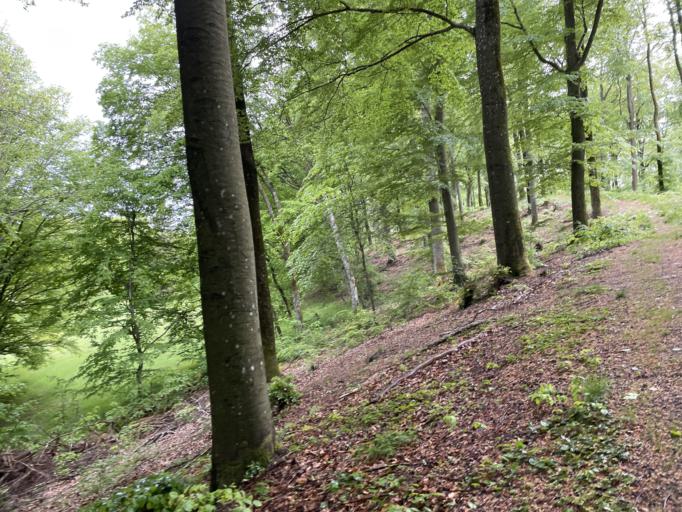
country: SE
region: Skane
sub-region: Hassleholms Kommun
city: Sosdala
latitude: 56.0601
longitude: 13.6731
